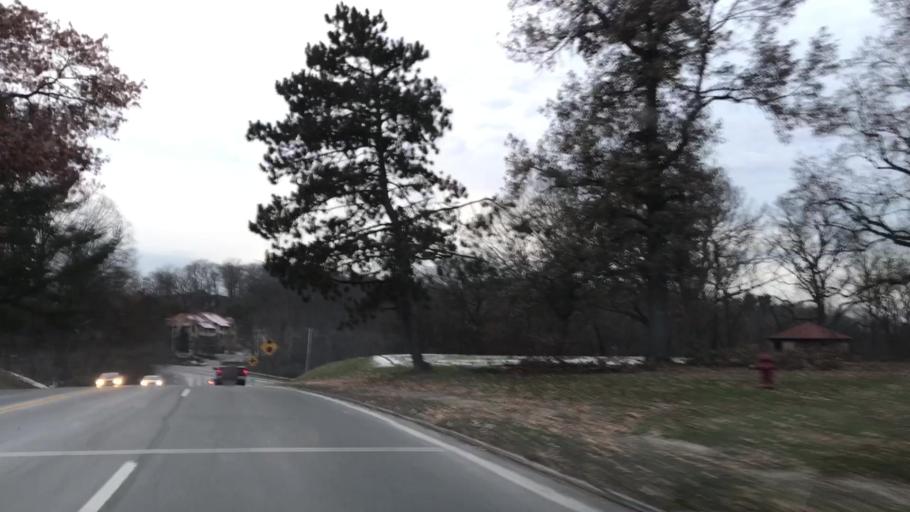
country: US
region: Pennsylvania
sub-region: Allegheny County
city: Allison Park
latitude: 40.5869
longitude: -79.9968
